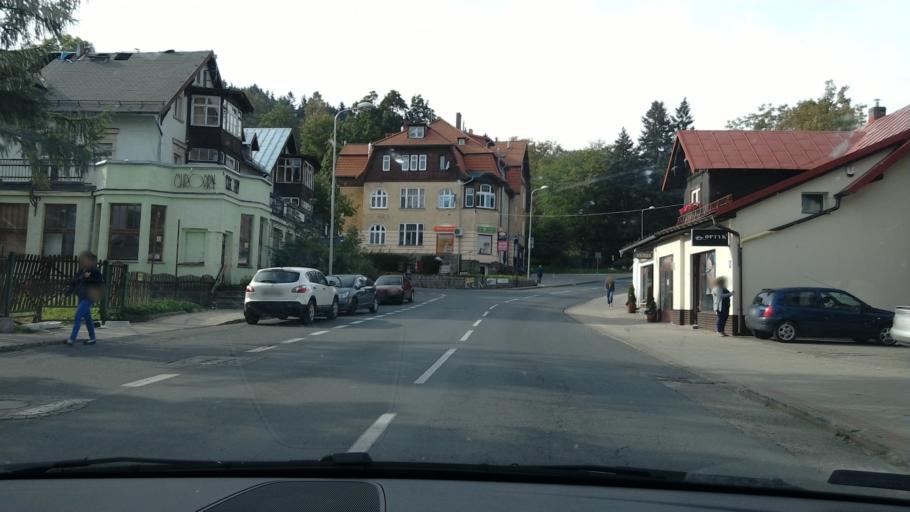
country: PL
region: Lower Silesian Voivodeship
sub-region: Powiat jeleniogorski
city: Karpacz
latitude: 50.7743
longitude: 15.7475
